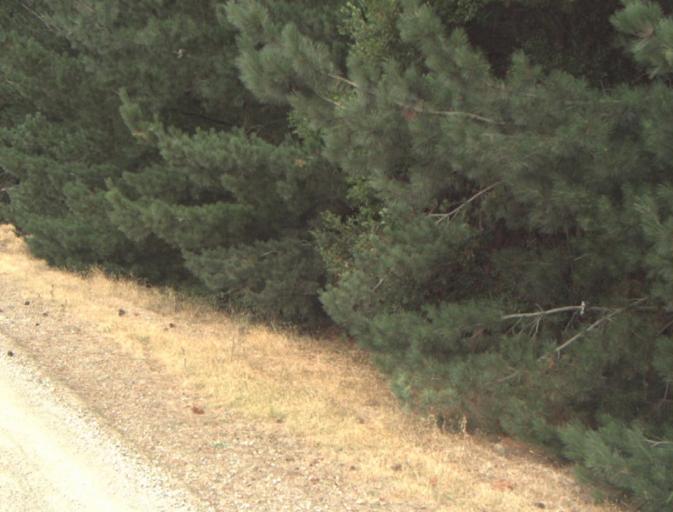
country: AU
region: Tasmania
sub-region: Launceston
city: Mayfield
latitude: -41.1663
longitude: 147.2121
